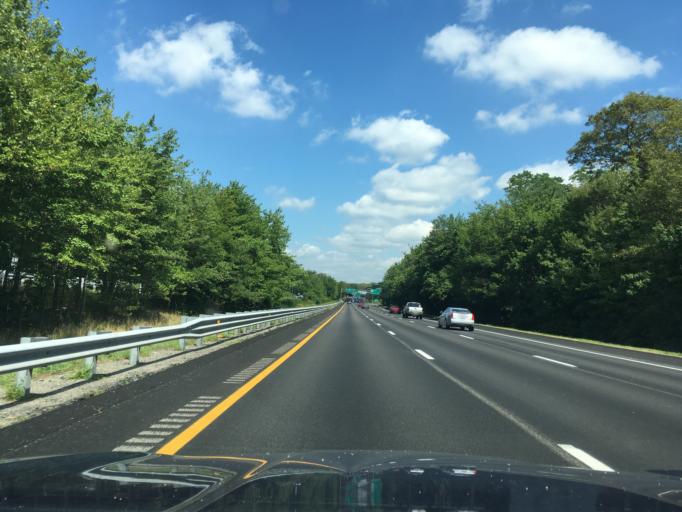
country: US
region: Rhode Island
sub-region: Kent County
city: East Greenwich
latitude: 41.6573
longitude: -71.4895
